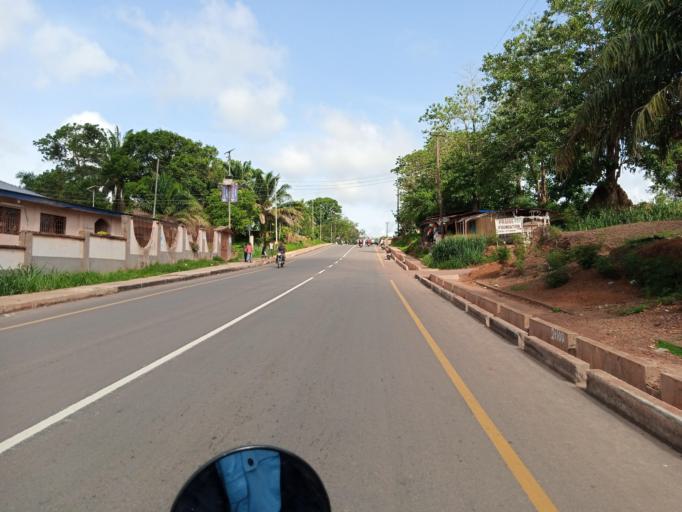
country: SL
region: Southern Province
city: Bo
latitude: 7.9568
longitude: -11.7256
